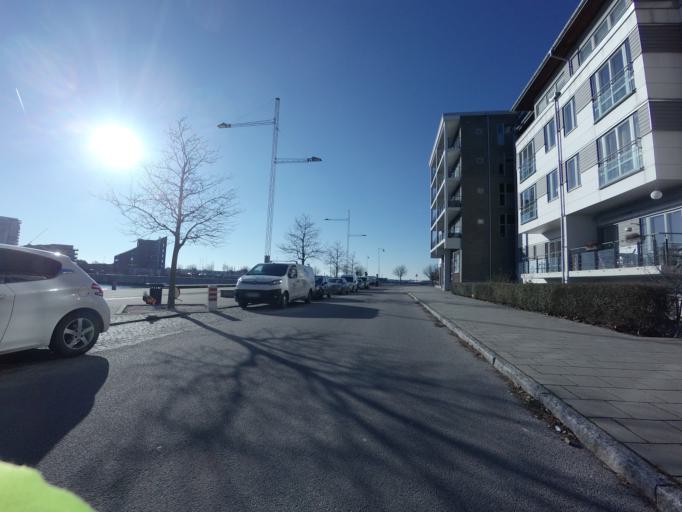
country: SE
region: Skane
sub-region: Malmo
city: Bunkeflostrand
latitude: 55.5913
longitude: 12.9232
